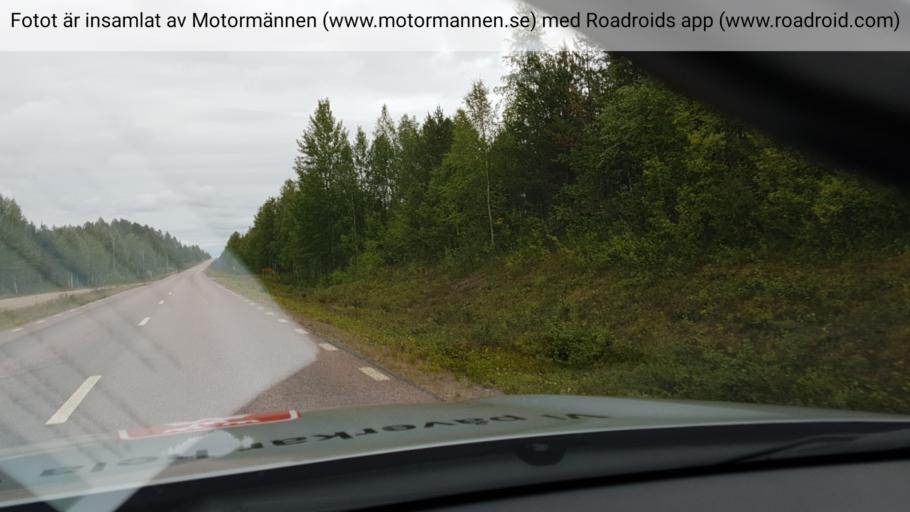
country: SE
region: Norrbotten
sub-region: Overkalix Kommun
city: OEverkalix
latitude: 67.0784
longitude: 22.5351
